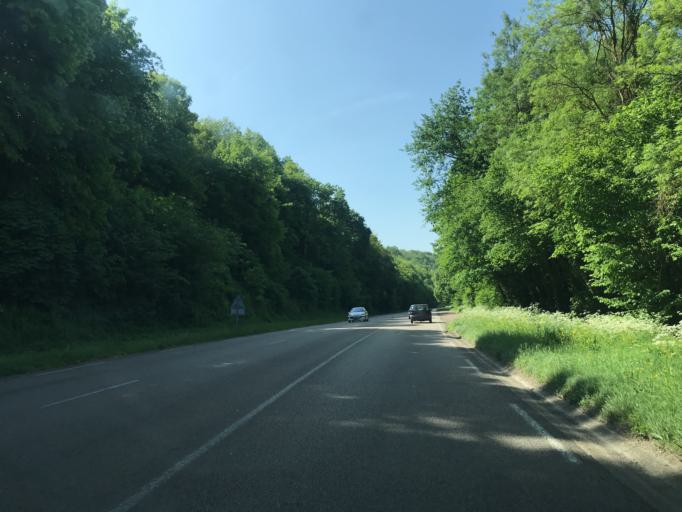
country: FR
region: Haute-Normandie
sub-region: Departement de la Seine-Maritime
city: Les Authieux-sur-le-Port-Saint-Ouen
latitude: 49.3475
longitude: 1.1271
